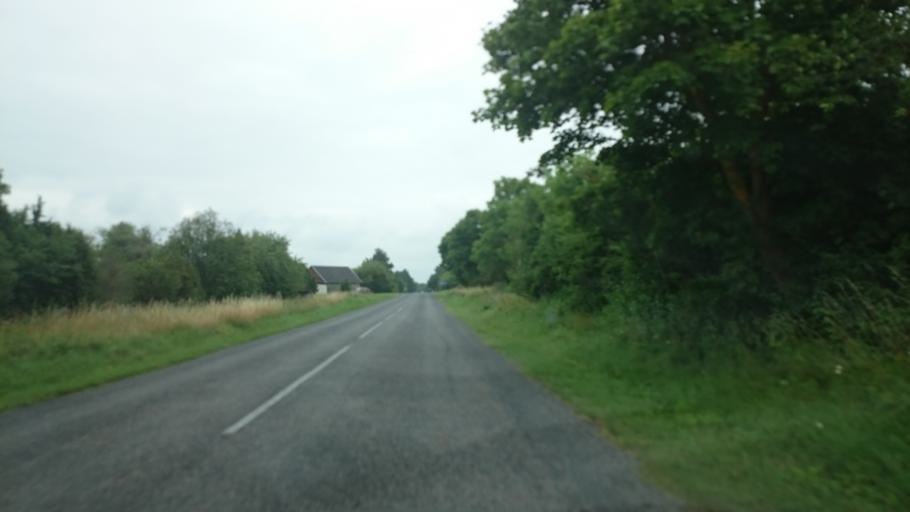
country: EE
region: Saare
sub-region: Orissaare vald
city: Orissaare
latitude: 58.5826
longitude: 23.0267
